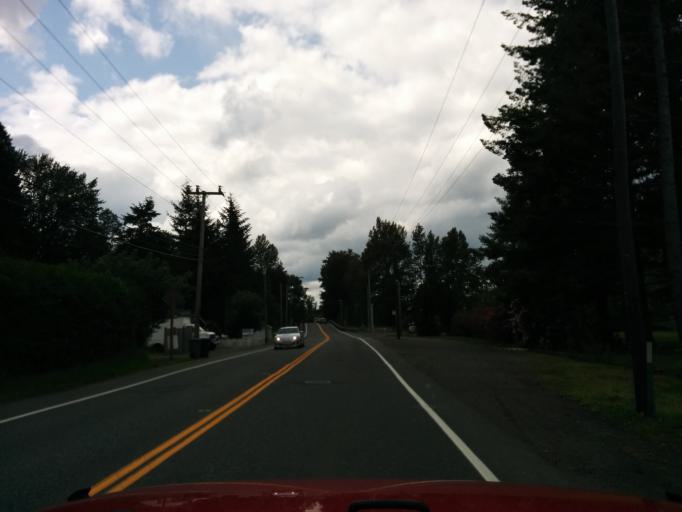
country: US
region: Washington
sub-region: King County
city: North Bend
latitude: 47.4984
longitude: -121.7858
